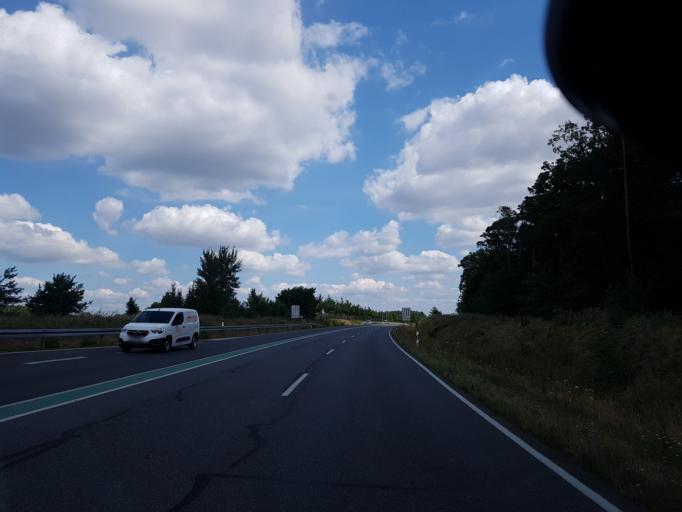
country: DE
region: Brandenburg
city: Drebkau
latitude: 51.6653
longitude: 14.2420
